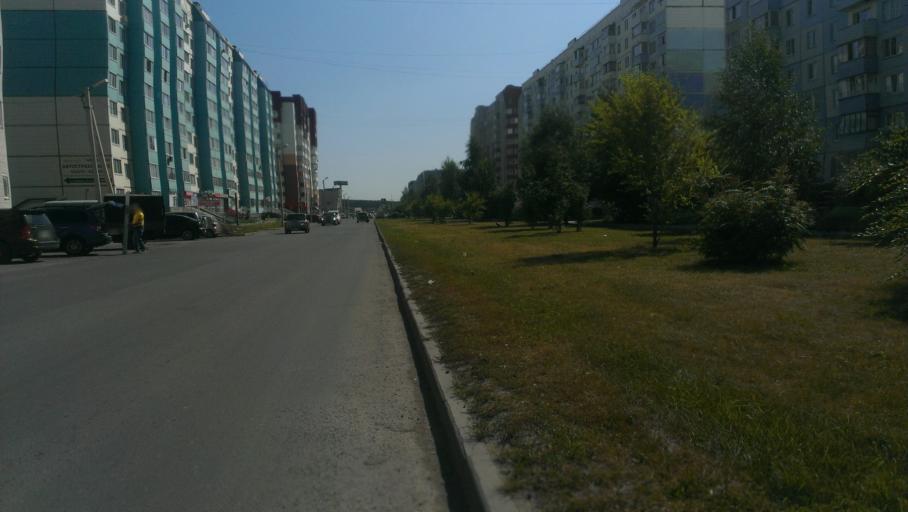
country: RU
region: Altai Krai
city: Novosilikatnyy
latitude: 53.3329
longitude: 83.6849
